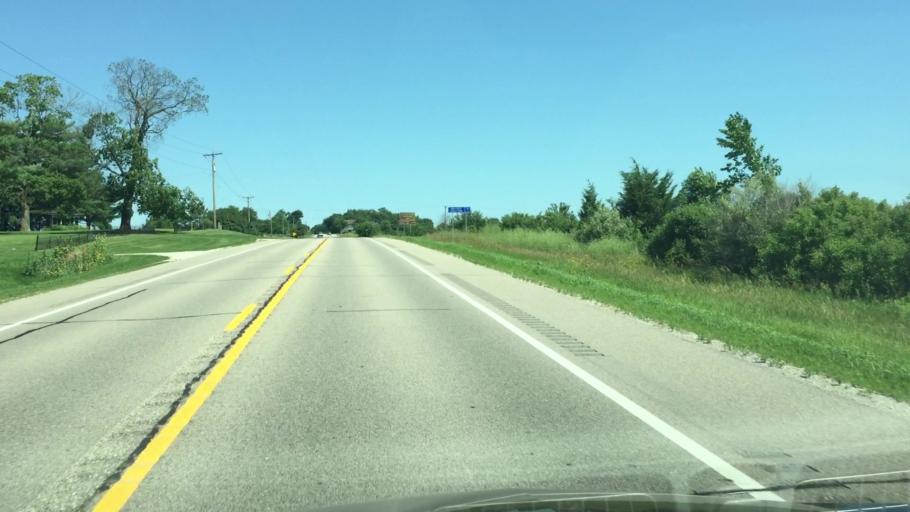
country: US
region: Iowa
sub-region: Johnson County
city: Solon
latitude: 41.8284
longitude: -91.4978
